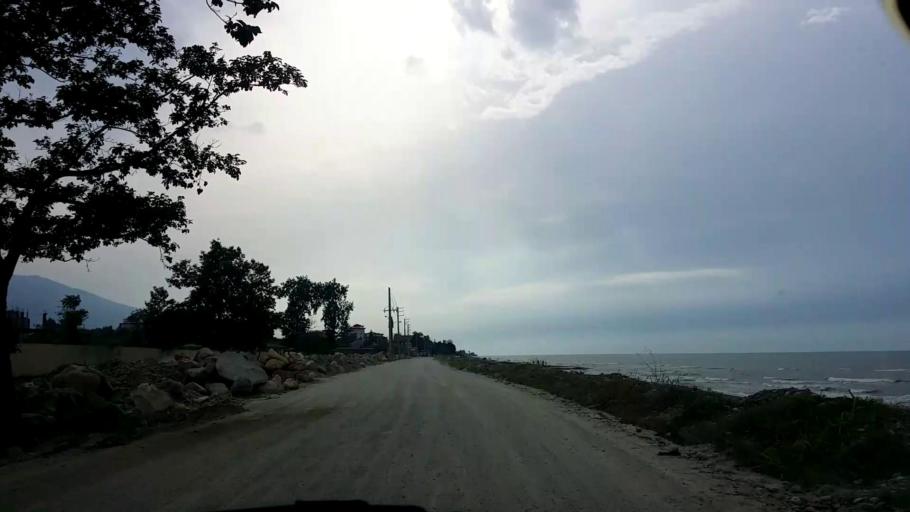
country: IR
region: Mazandaran
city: Chalus
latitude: 36.6854
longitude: 51.4257
